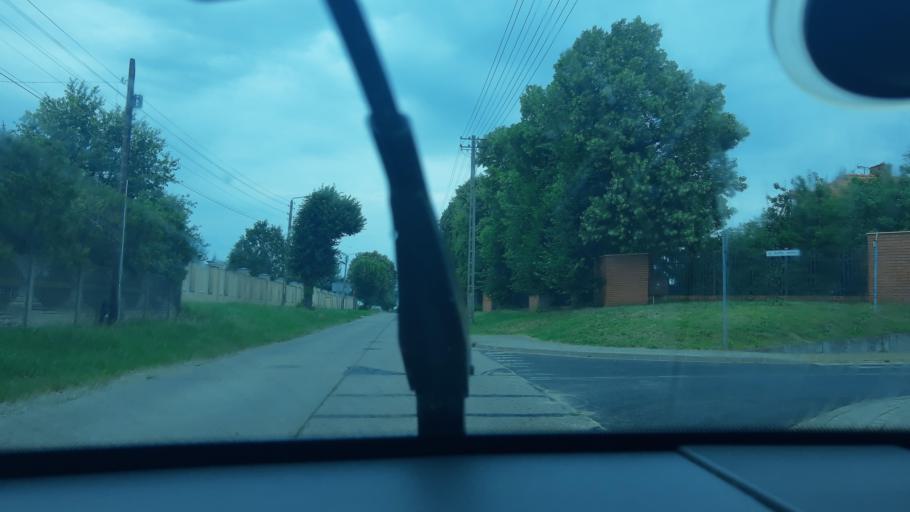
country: PL
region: Lodz Voivodeship
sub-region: Powiat sieradzki
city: Sieradz
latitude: 51.5752
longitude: 18.7368
